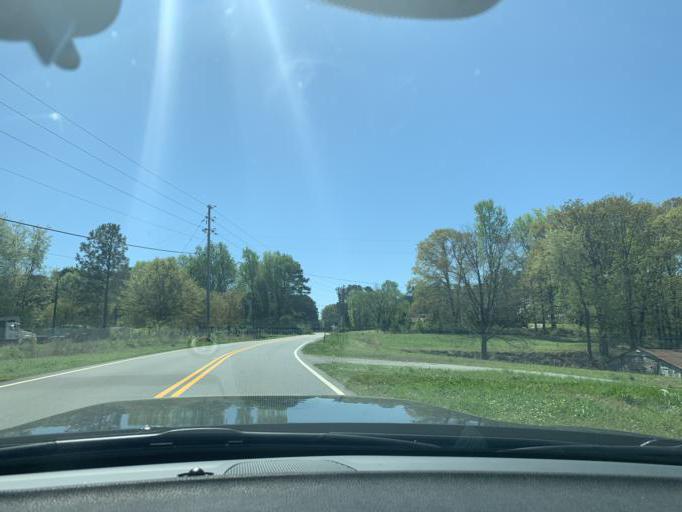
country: US
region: Georgia
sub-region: Forsyth County
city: Cumming
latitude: 34.1860
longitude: -84.1725
